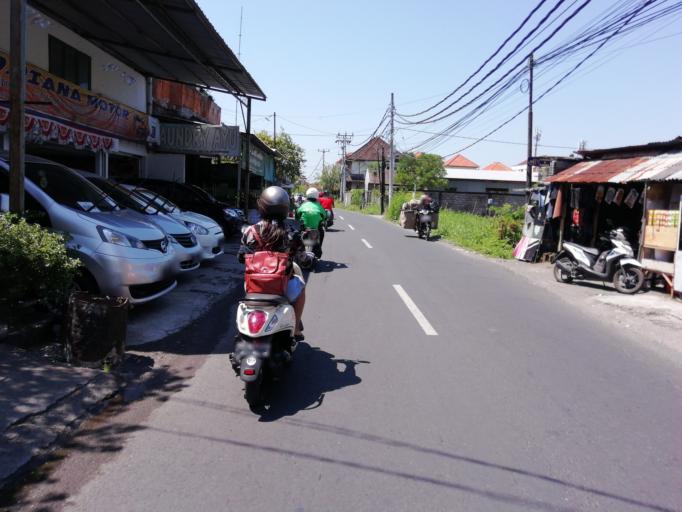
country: ID
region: Bali
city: Karyadharma
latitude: -8.6952
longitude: 115.1898
